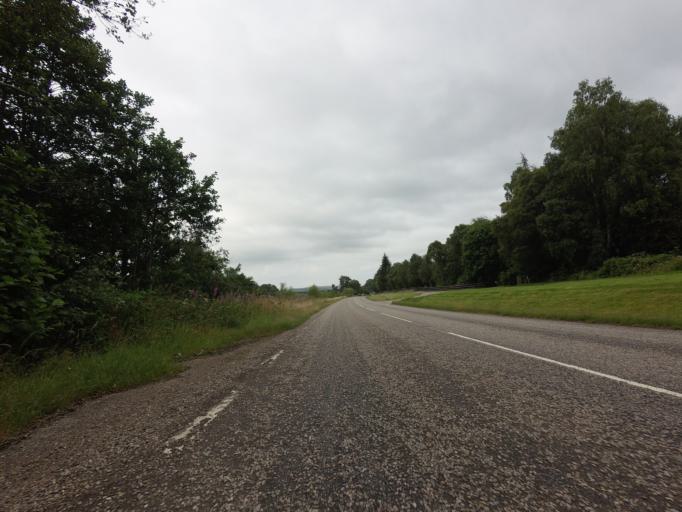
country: GB
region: Scotland
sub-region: Highland
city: Evanton
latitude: 57.9203
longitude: -4.3981
